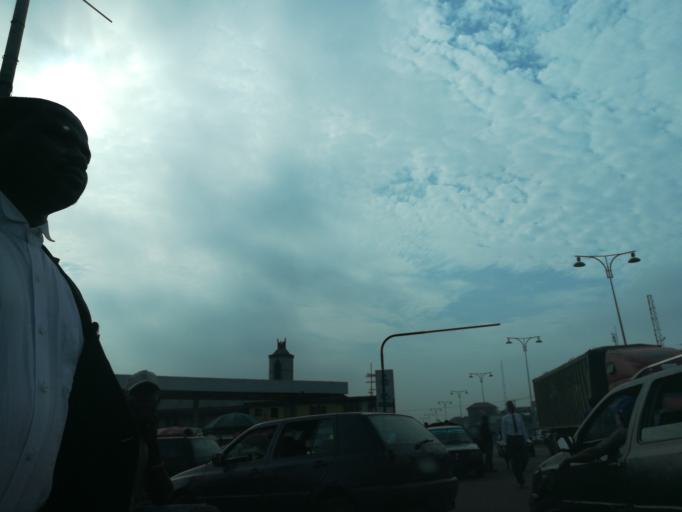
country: NG
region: Rivers
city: Port Harcourt
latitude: 4.7987
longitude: 6.9923
